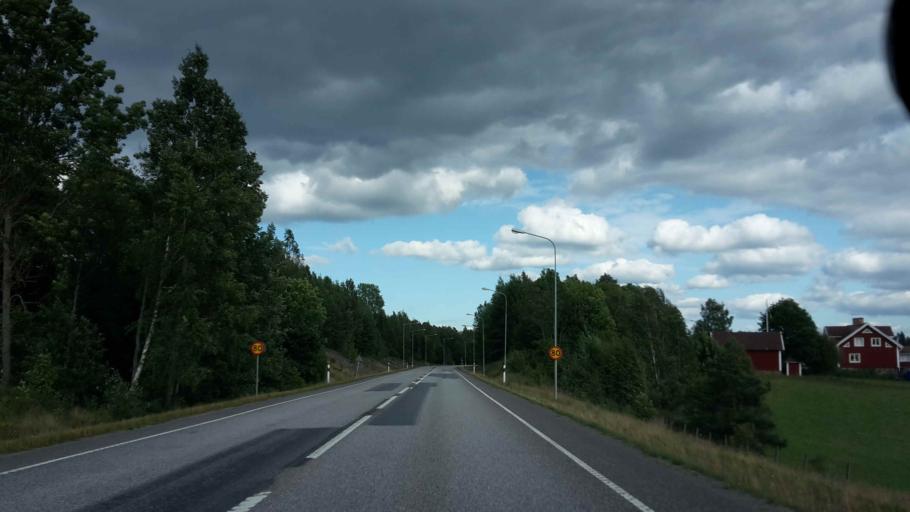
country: SE
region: OEstergoetland
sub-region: Linkopings Kommun
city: Ljungsbro
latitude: 58.7907
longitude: 15.4748
